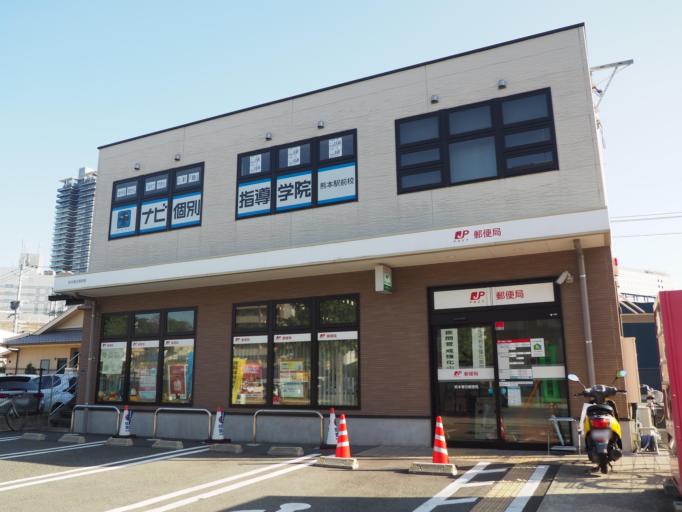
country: JP
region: Kumamoto
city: Kumamoto
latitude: 32.7923
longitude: 130.6884
